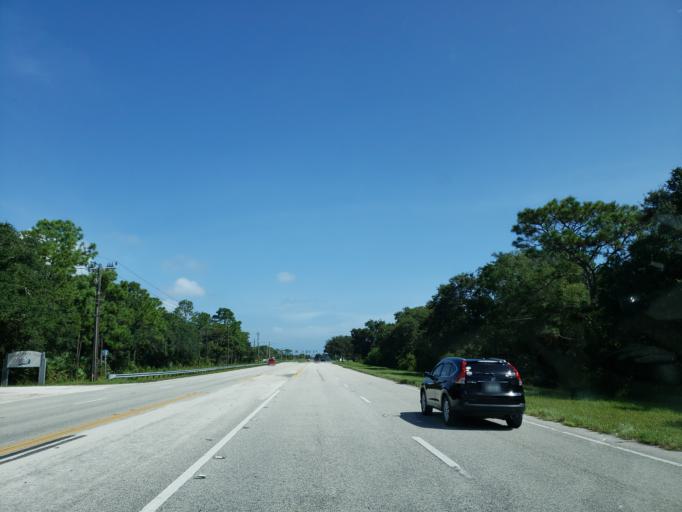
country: US
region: Florida
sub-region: Brevard County
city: West Melbourne
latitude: 28.0903
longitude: -80.6547
